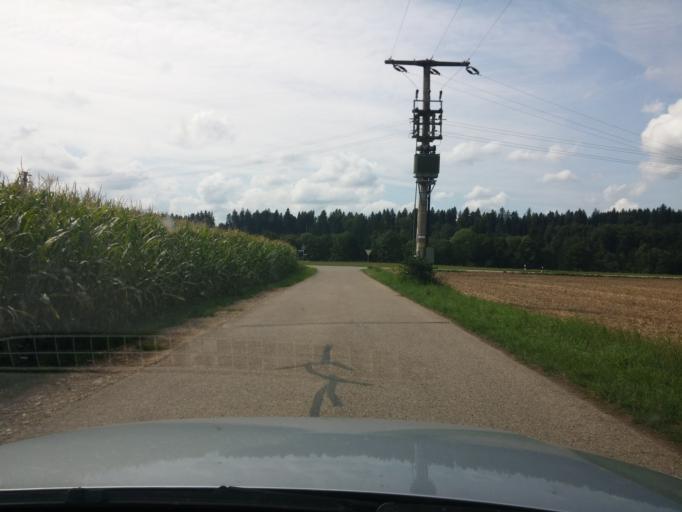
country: DE
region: Bavaria
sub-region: Swabia
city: Lautrach
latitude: 47.8897
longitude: 10.1138
